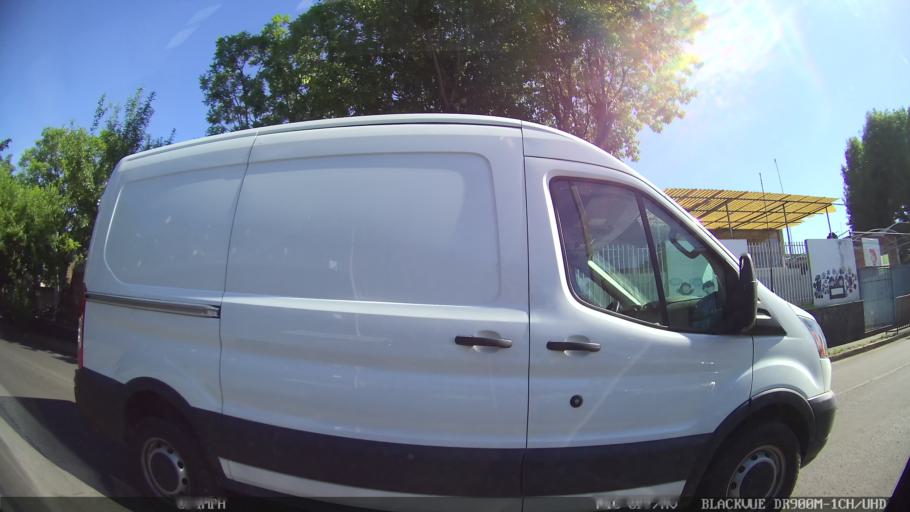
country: MX
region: Jalisco
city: Tlaquepaque
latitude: 20.6646
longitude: -103.3035
